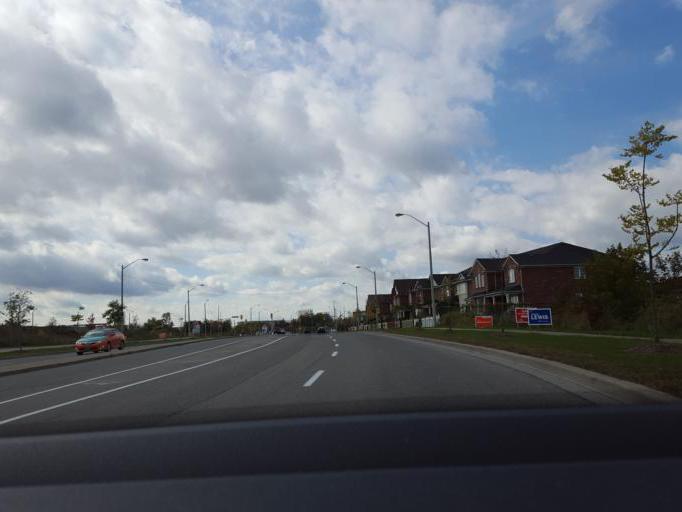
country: CA
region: Ontario
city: Scarborough
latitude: 43.8201
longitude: -79.2184
